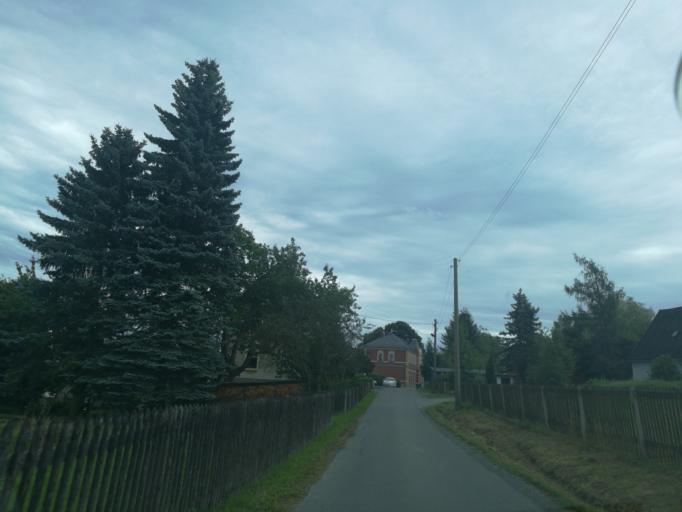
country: DE
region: Saxony
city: Adorf
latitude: 50.3101
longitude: 12.2758
